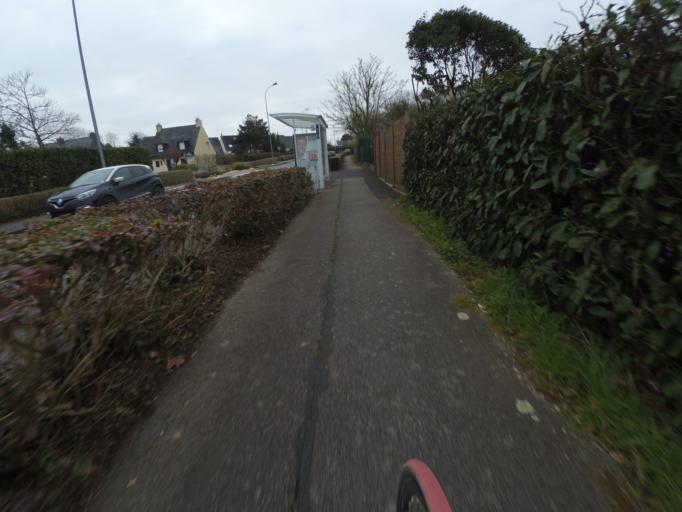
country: FR
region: Pays de la Loire
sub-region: Departement de la Loire-Atlantique
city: Carquefou
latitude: 47.2778
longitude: -1.4843
